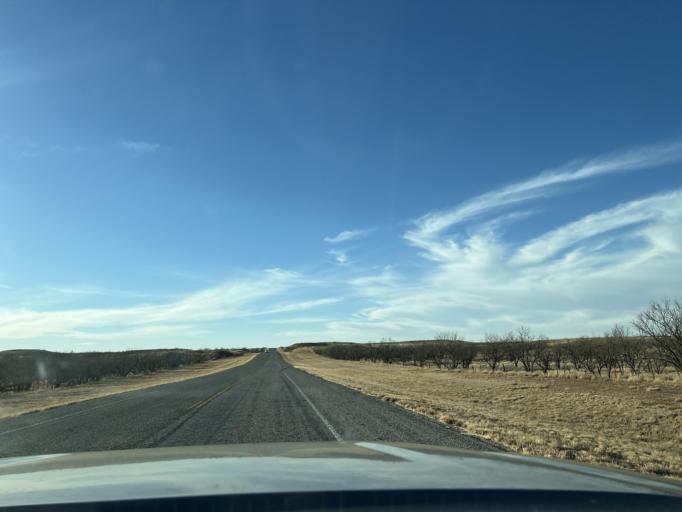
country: US
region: Texas
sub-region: Borden County
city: Gail
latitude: 32.7571
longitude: -101.2489
